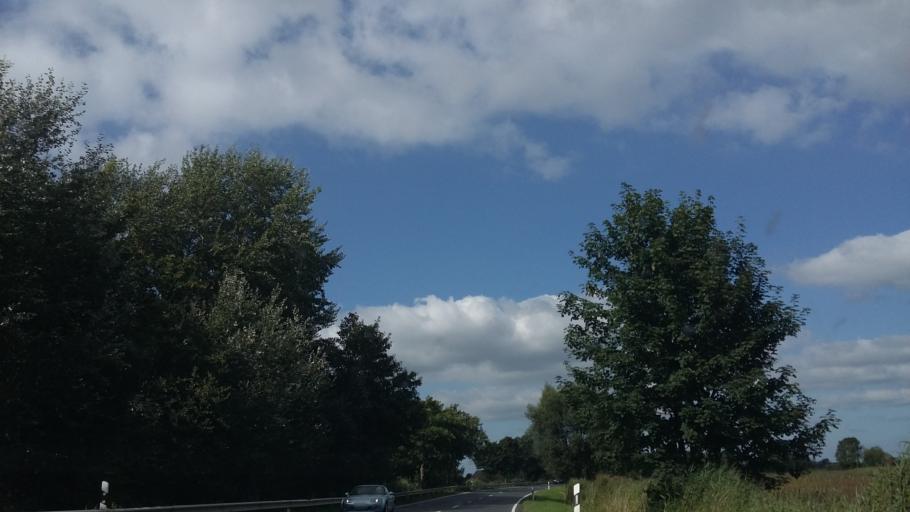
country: DE
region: Lower Saxony
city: Loxstedt
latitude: 53.4717
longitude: 8.5971
